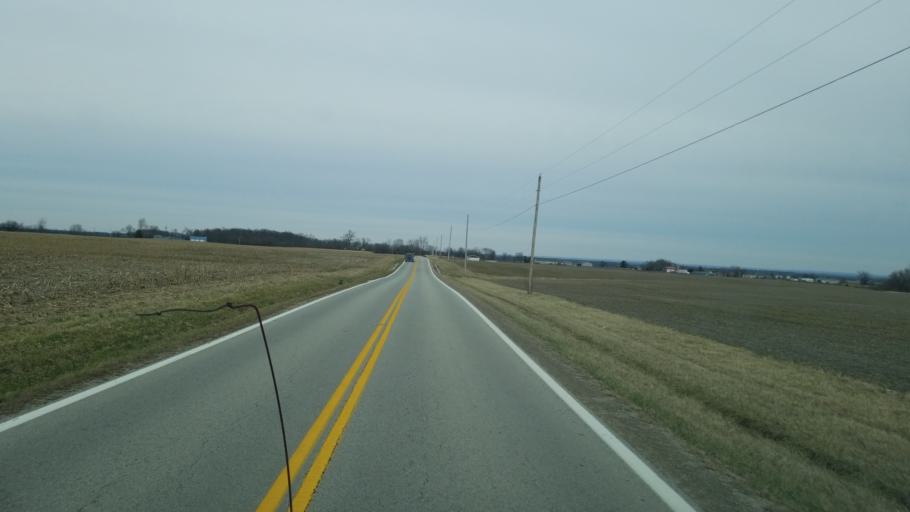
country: US
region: Ohio
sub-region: Ross County
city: Frankfort
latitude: 39.4802
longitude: -83.1872
